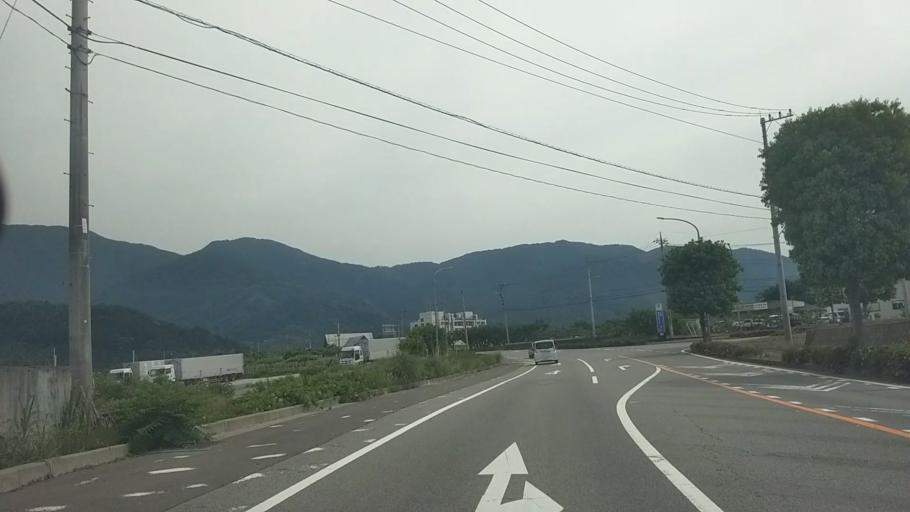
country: JP
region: Yamanashi
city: Isawa
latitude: 35.5847
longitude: 138.5905
